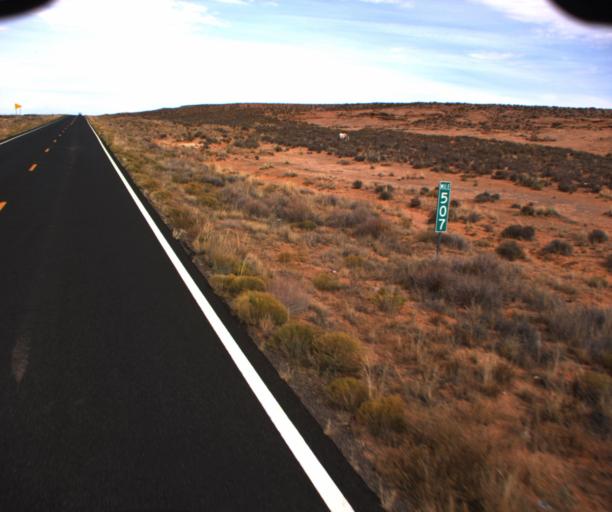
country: US
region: Arizona
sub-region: Apache County
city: Many Farms
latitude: 36.8787
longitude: -109.6298
